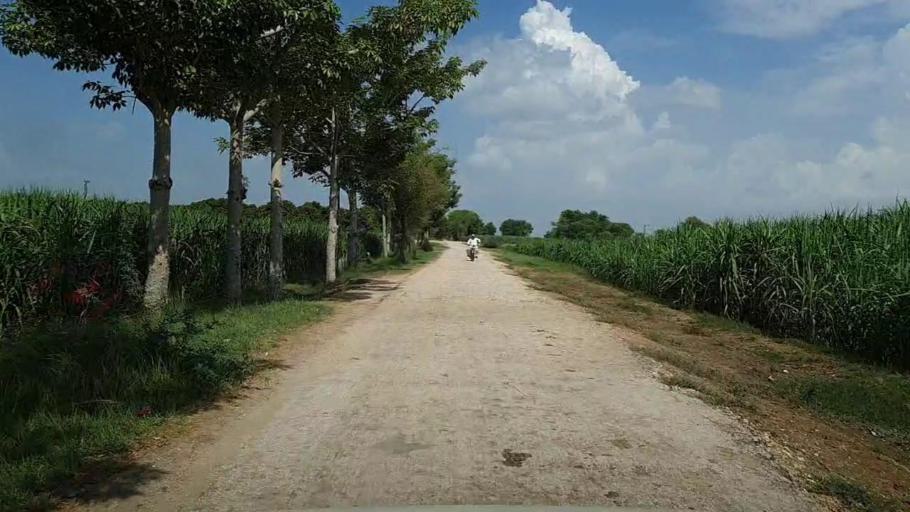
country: PK
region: Sindh
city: Bhiria
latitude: 26.9178
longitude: 68.2357
